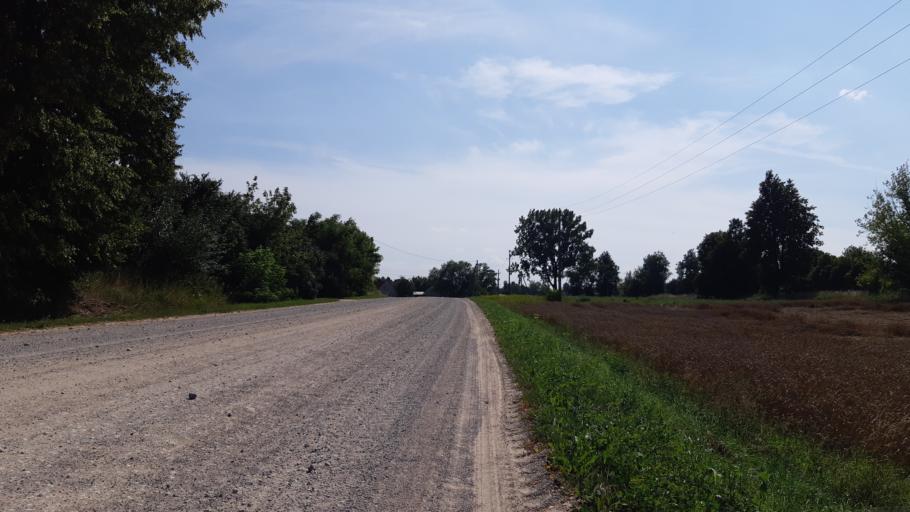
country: LT
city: Virbalis
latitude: 54.6321
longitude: 22.8257
